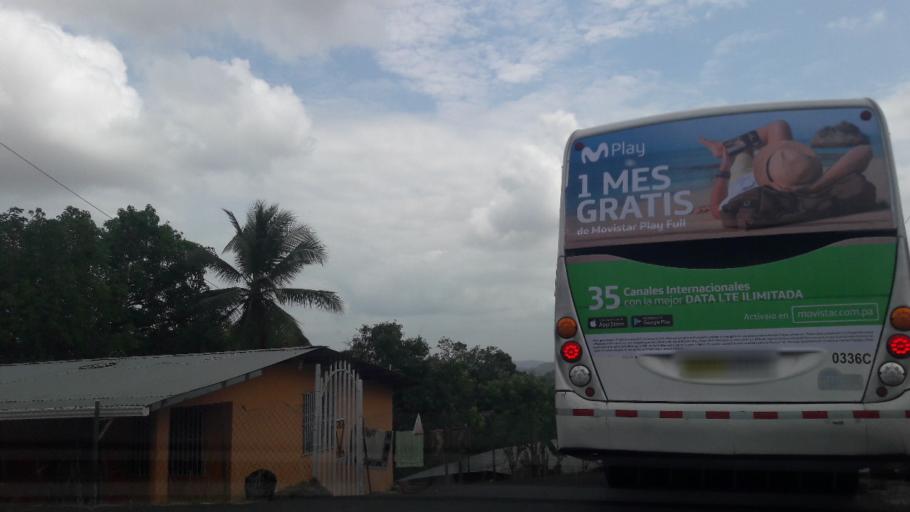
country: PA
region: Panama
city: Alcalde Diaz
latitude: 9.1259
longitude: -79.5549
